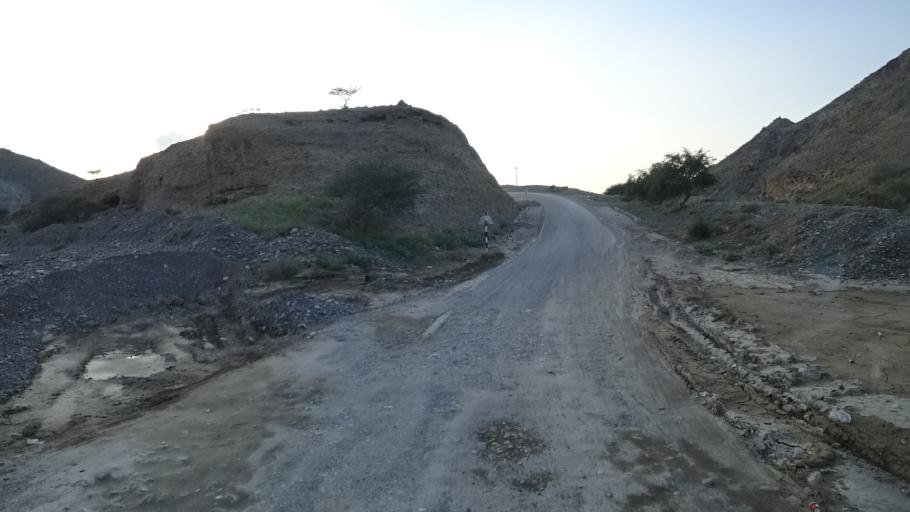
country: OM
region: Al Batinah
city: Al Khaburah
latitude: 23.7947
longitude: 56.9705
